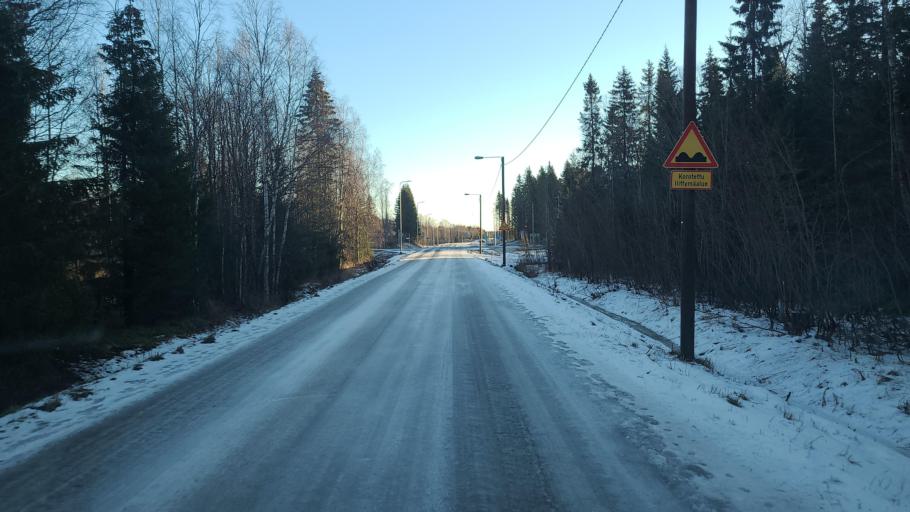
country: FI
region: Lapland
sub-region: Kemi-Tornio
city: Kemi
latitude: 65.6804
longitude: 24.7391
